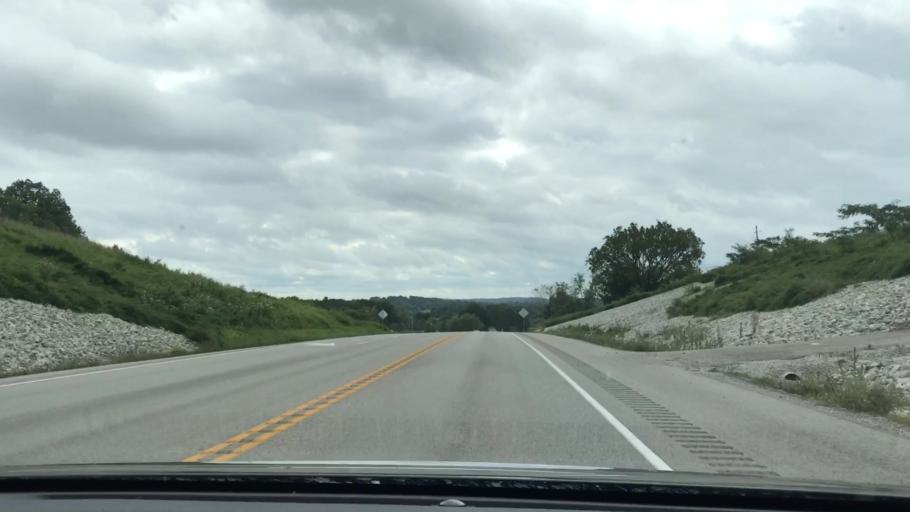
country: US
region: Kentucky
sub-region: Barren County
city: Glasgow
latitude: 36.9497
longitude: -85.8458
